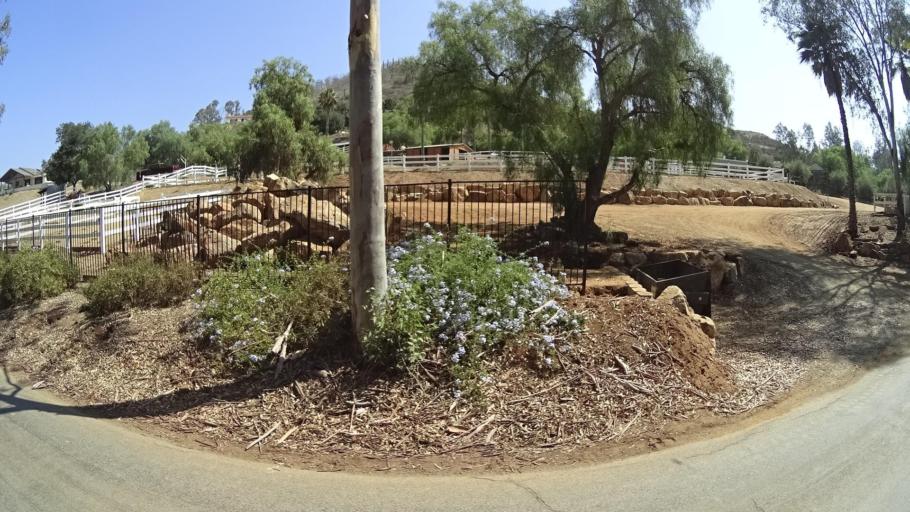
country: US
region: California
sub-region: San Diego County
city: Bonsall
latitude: 33.2658
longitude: -117.2275
